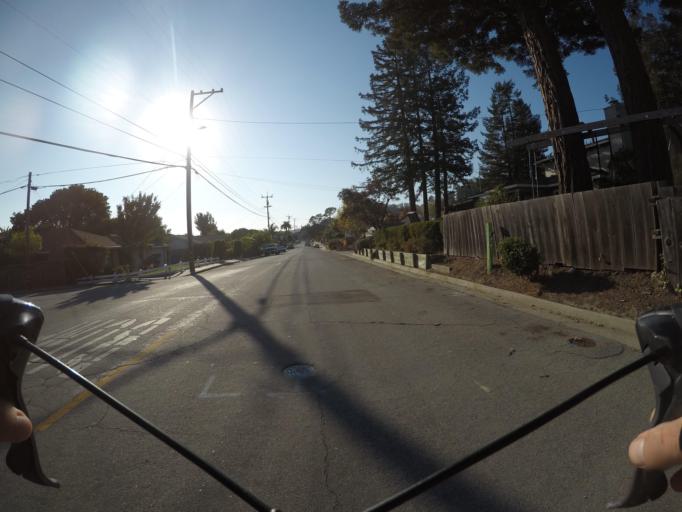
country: US
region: California
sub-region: Santa Cruz County
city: Live Oak
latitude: 36.9907
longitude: -121.9904
